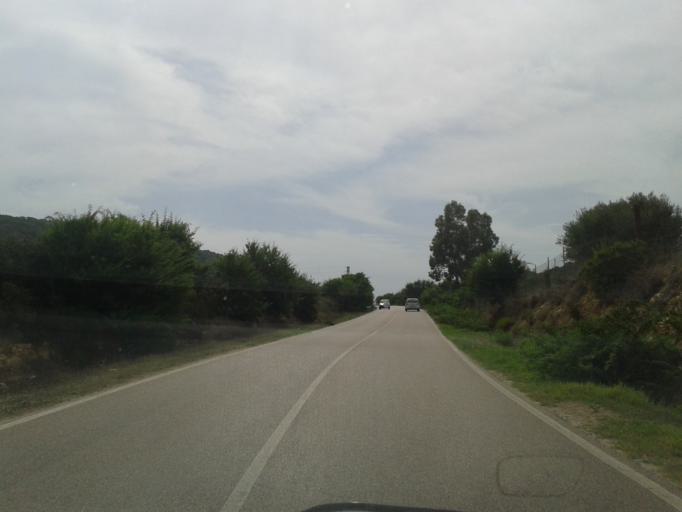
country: IT
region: Sardinia
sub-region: Provincia di Cagliari
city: Villasimius
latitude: 39.1439
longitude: 9.5283
